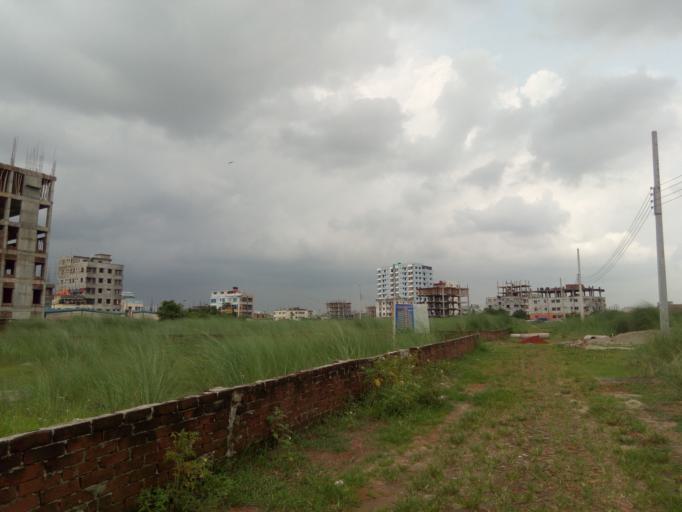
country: BD
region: Dhaka
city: Azimpur
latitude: 23.7507
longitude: 90.3503
